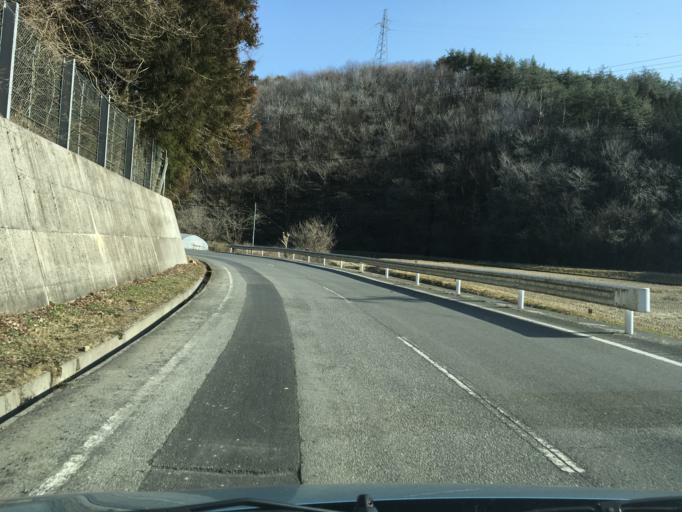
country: JP
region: Miyagi
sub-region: Oshika Gun
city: Onagawa Cho
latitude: 38.7875
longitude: 141.4543
